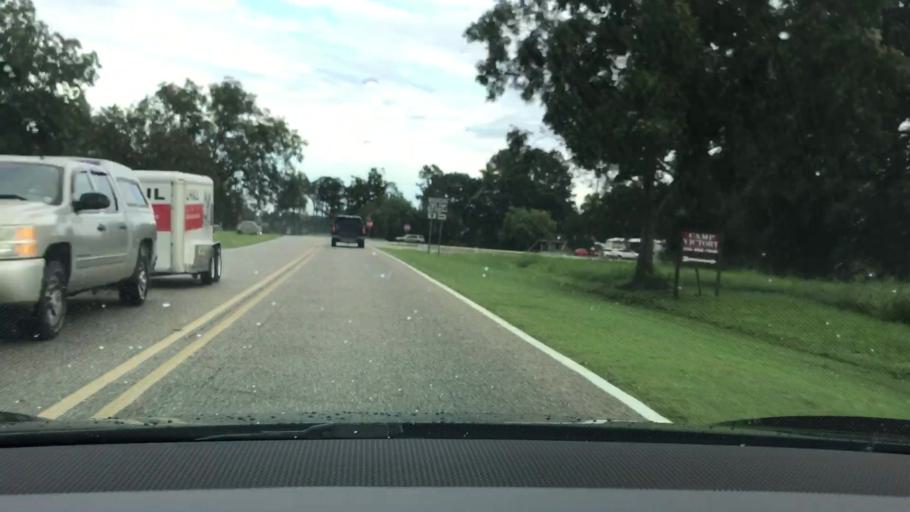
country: US
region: Alabama
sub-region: Geneva County
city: Samson
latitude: 31.1172
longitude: -86.1210
